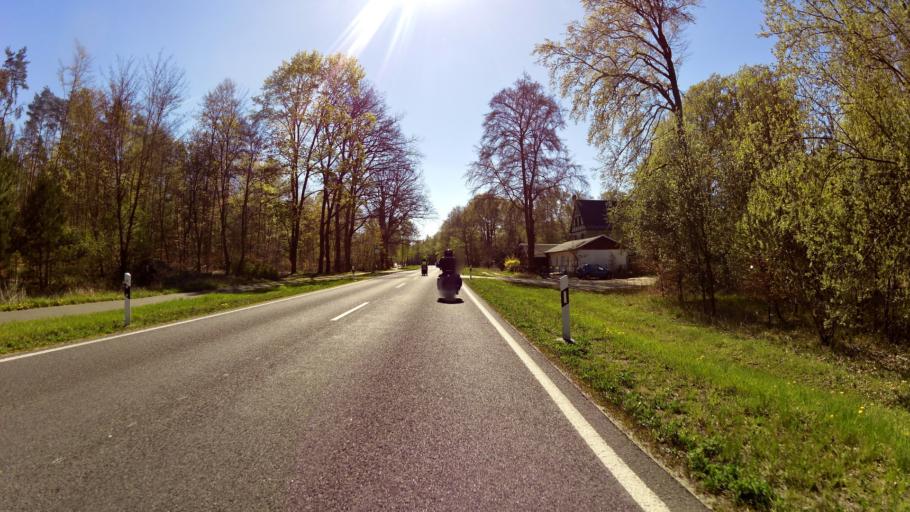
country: DE
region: Brandenburg
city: Wandlitz
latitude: 52.7171
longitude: 13.5251
